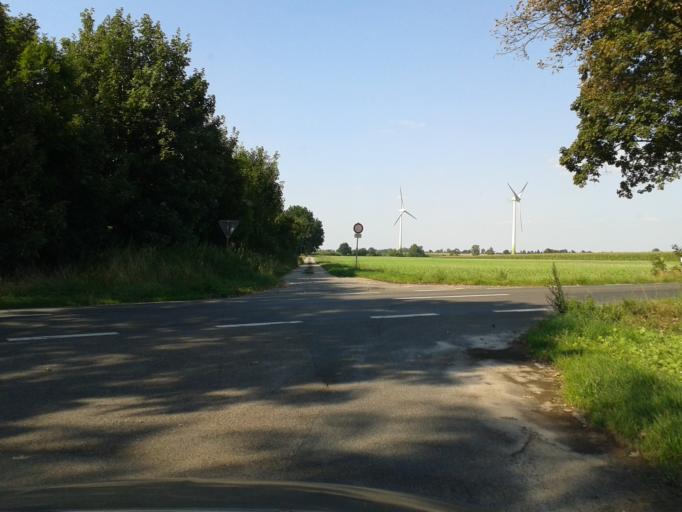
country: DE
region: Lower Saxony
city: Lubbow
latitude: 52.9181
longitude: 11.1879
